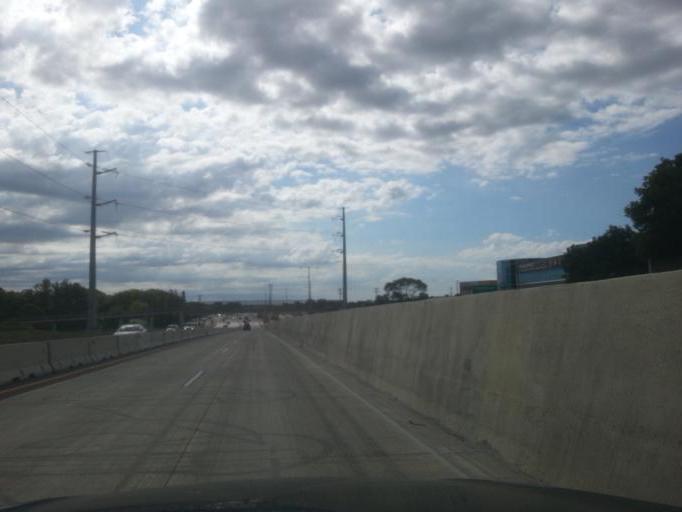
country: US
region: Wisconsin
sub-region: Dane County
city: Shorewood Hills
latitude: 43.0408
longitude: -89.4614
